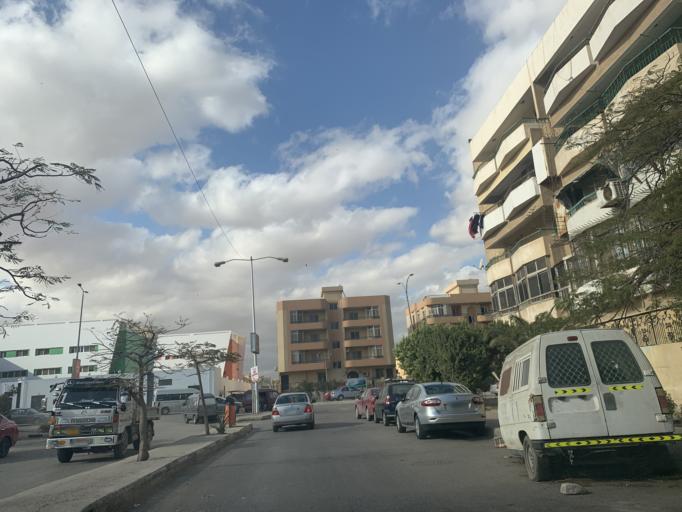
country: EG
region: Al Jizah
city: Madinat Sittah Uktubar
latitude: 29.9851
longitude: 30.9371
